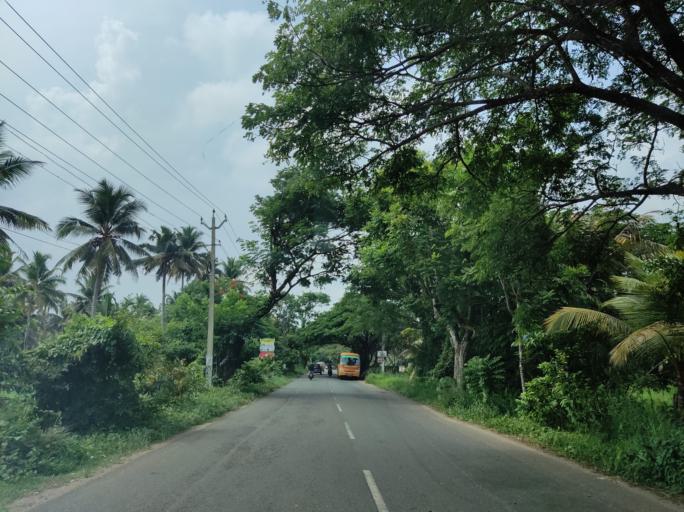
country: IN
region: Kerala
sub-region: Alappuzha
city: Shertallai
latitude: 9.6246
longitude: 76.4296
